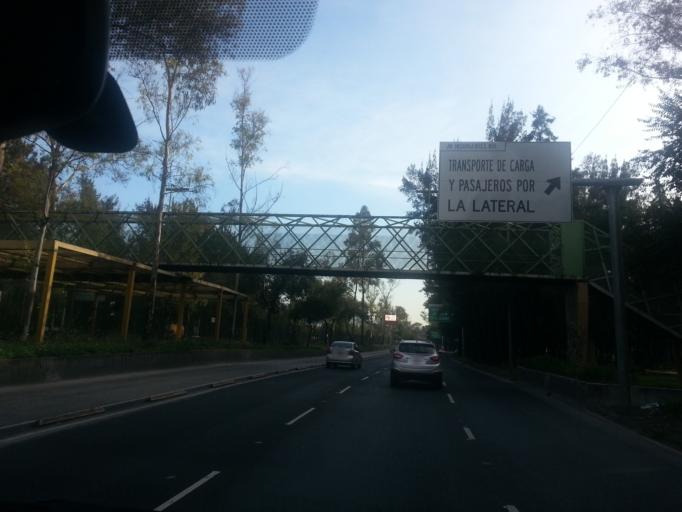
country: MX
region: Mexico
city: Colonia Lindavista
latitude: 19.4784
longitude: -99.1307
